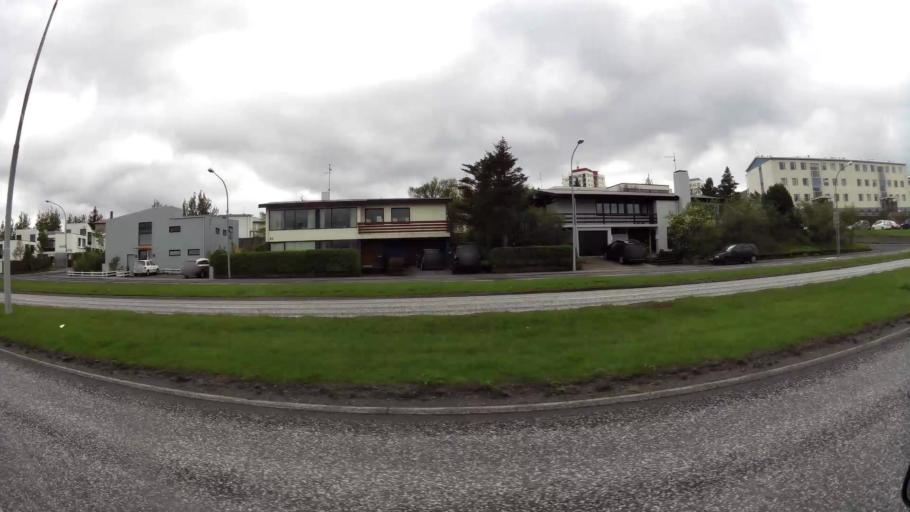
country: IS
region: Capital Region
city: Reykjavik
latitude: 64.1472
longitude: -21.8608
